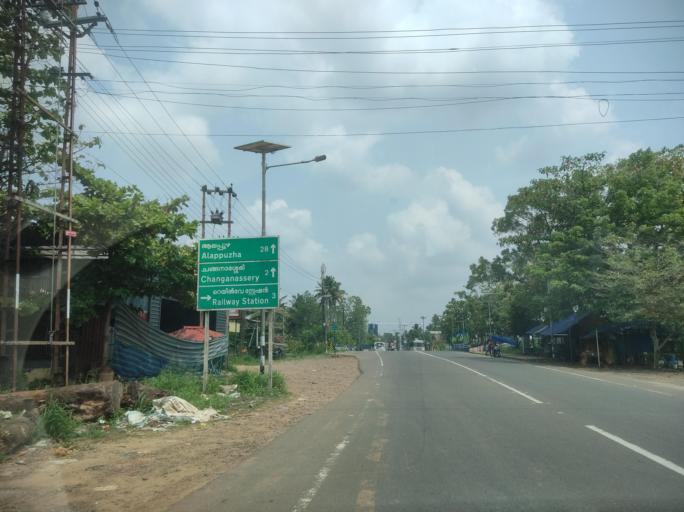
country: IN
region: Kerala
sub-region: Kottayam
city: Changanacheri
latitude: 9.4286
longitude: 76.5450
